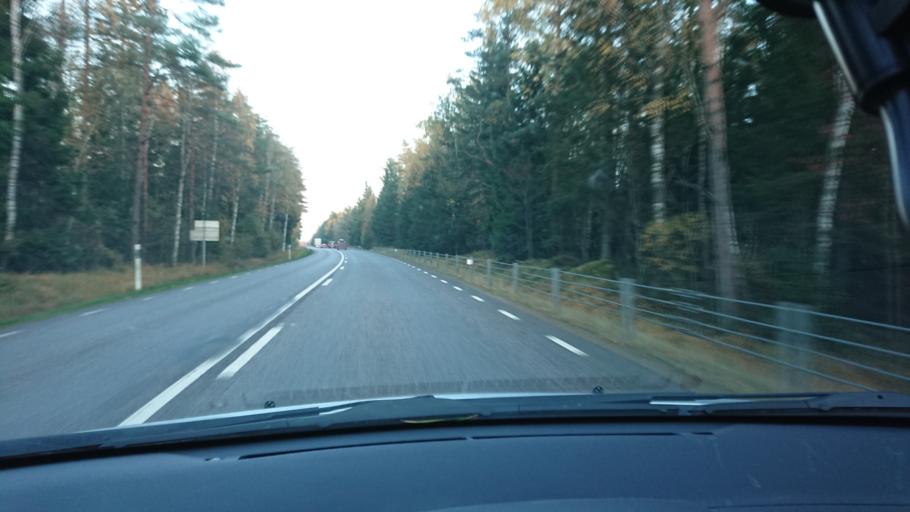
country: SE
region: Halland
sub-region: Laholms Kommun
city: Veinge
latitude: 56.7146
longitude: 13.2024
